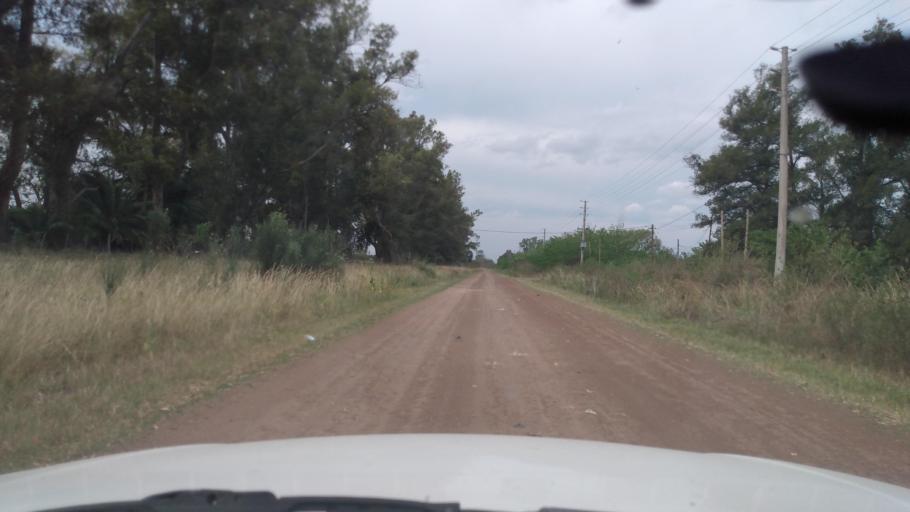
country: AR
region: Buenos Aires
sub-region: Partido de Lujan
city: Lujan
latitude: -34.5533
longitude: -59.1738
